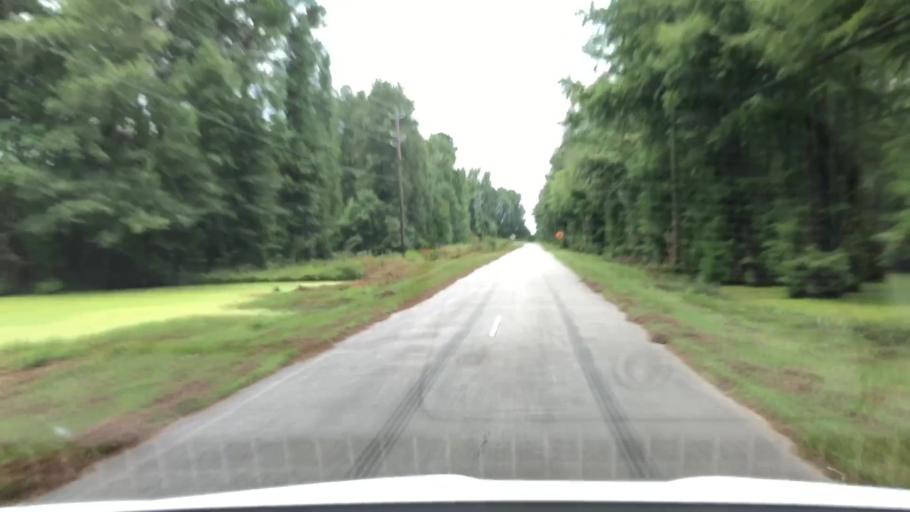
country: US
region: North Carolina
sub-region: Lenoir County
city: Kinston
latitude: 35.2588
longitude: -77.5958
